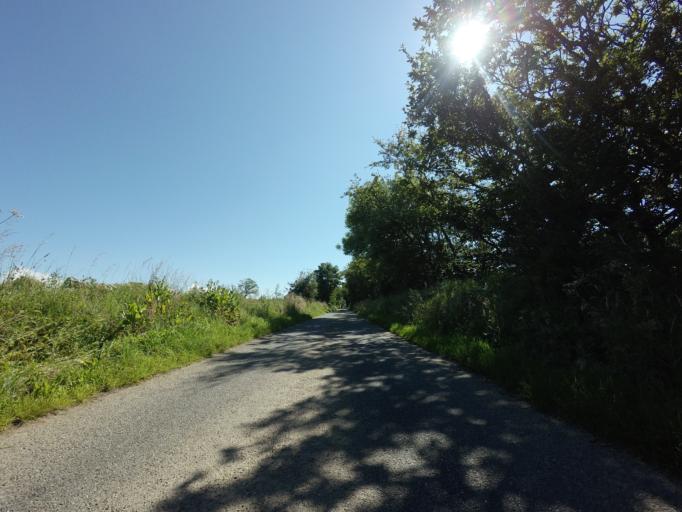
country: GB
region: Scotland
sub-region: Aberdeenshire
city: Macduff
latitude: 57.6516
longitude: -2.5028
